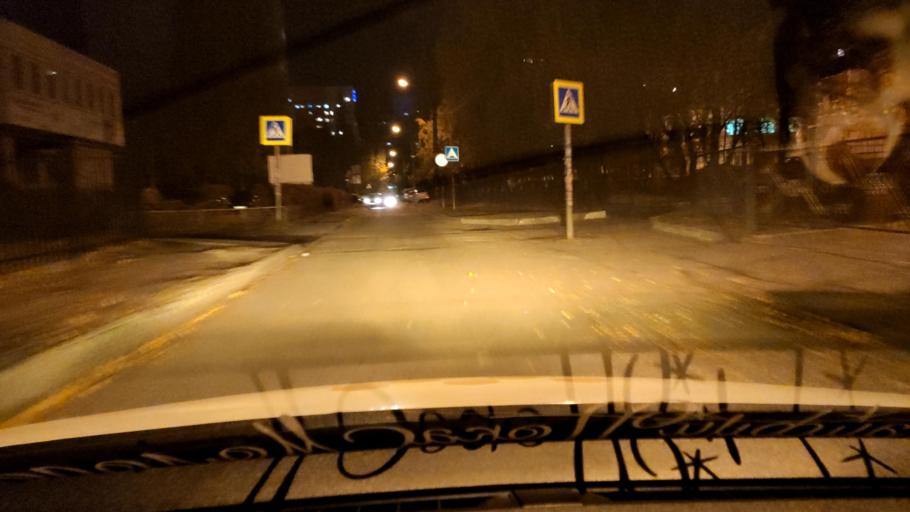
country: RU
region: Voronezj
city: Podgornoye
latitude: 51.7094
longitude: 39.1550
